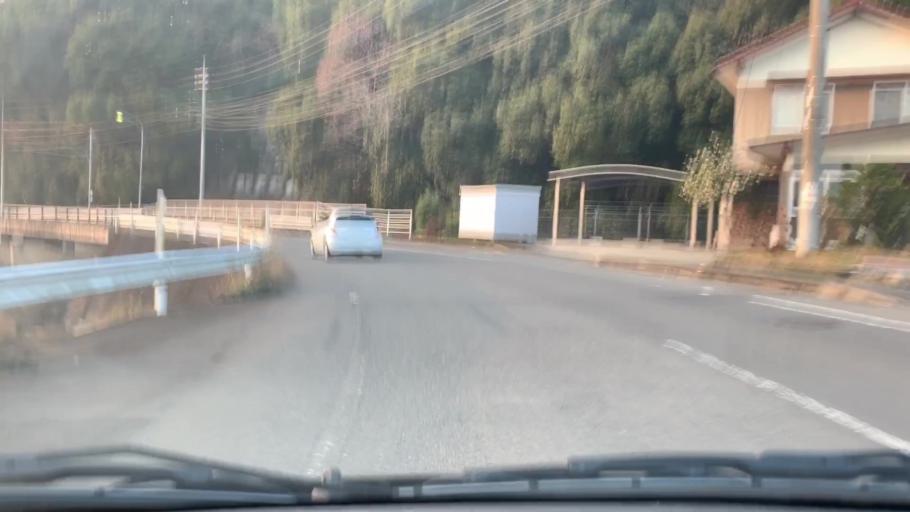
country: JP
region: Saga Prefecture
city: Imaricho-ko
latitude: 33.2718
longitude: 129.8945
